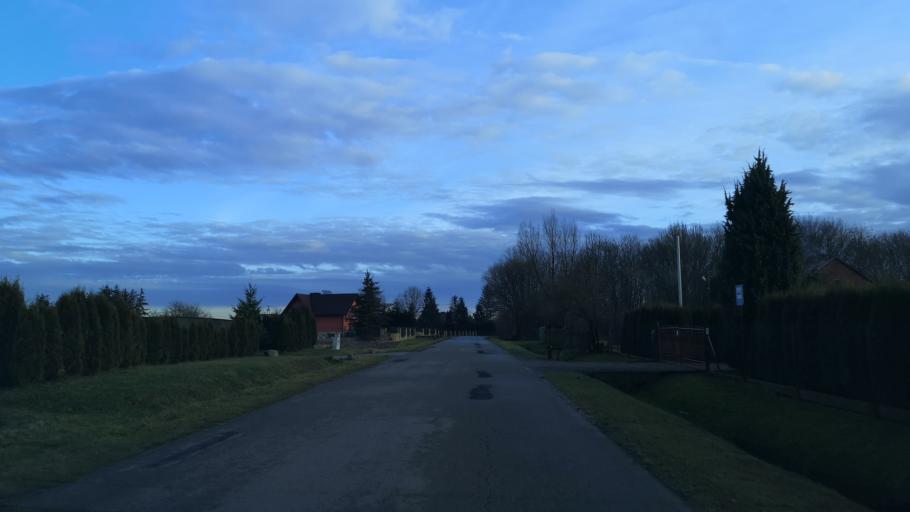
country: PL
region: Subcarpathian Voivodeship
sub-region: Powiat przeworski
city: Adamowka
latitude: 50.2444
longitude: 22.6335
